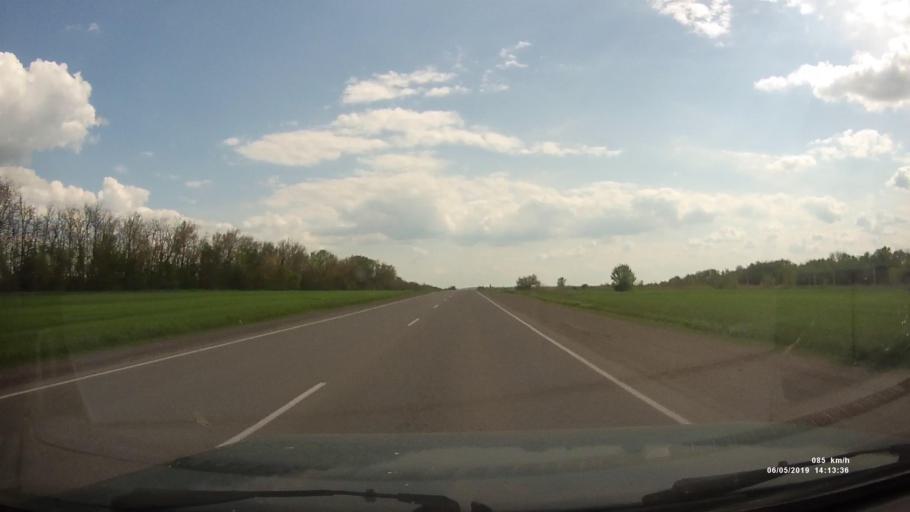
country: RU
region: Rostov
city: Kamenolomni
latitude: 47.6587
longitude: 40.2931
